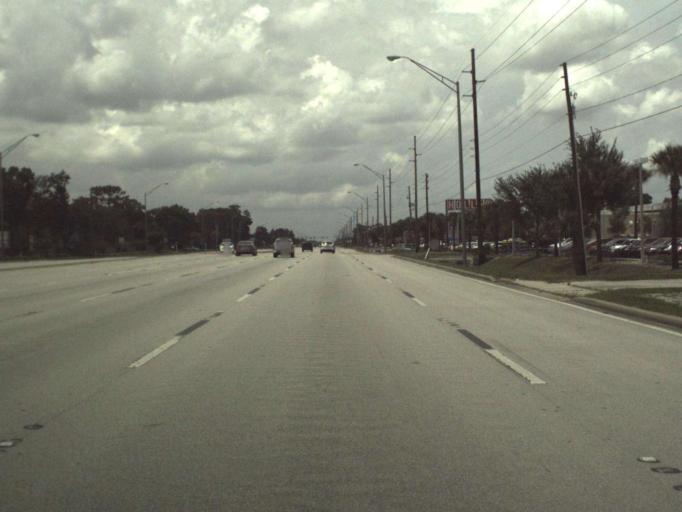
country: US
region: Florida
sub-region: Seminole County
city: Goldenrod
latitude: 28.6128
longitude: -81.3098
